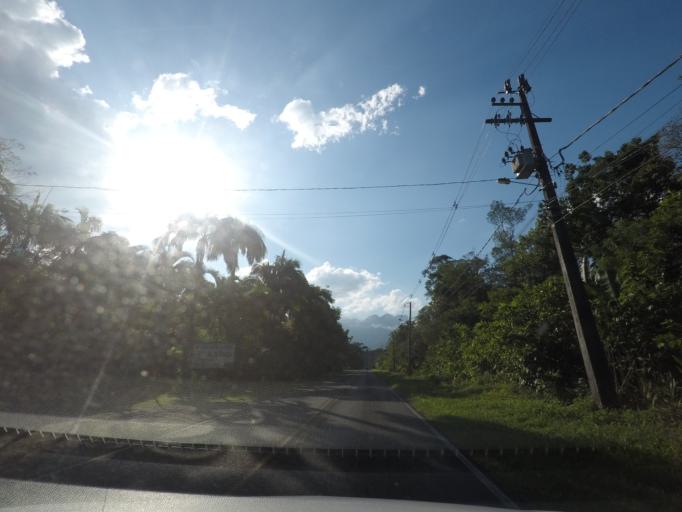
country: BR
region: Parana
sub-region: Antonina
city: Antonina
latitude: -25.4329
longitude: -48.8729
